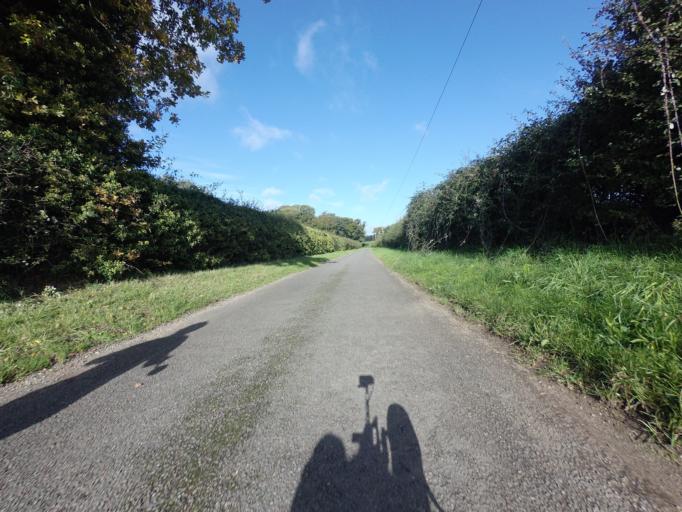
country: GB
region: England
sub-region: Norfolk
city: Dersingham
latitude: 52.8493
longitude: 0.6724
